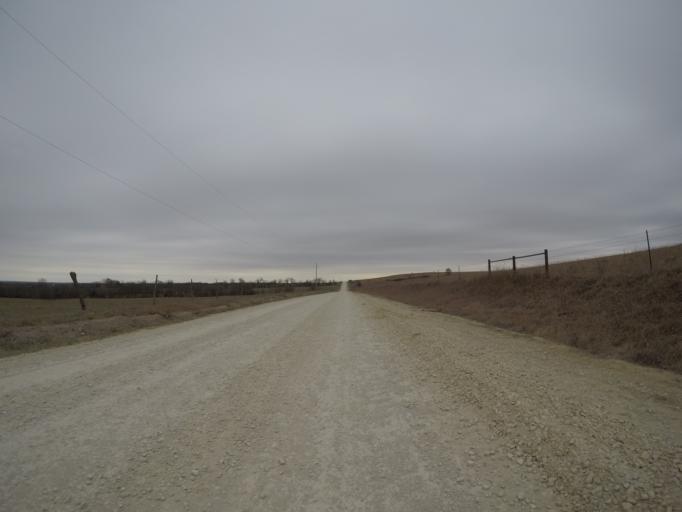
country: US
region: Kansas
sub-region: Wabaunsee County
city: Alma
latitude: 38.8519
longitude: -96.1133
